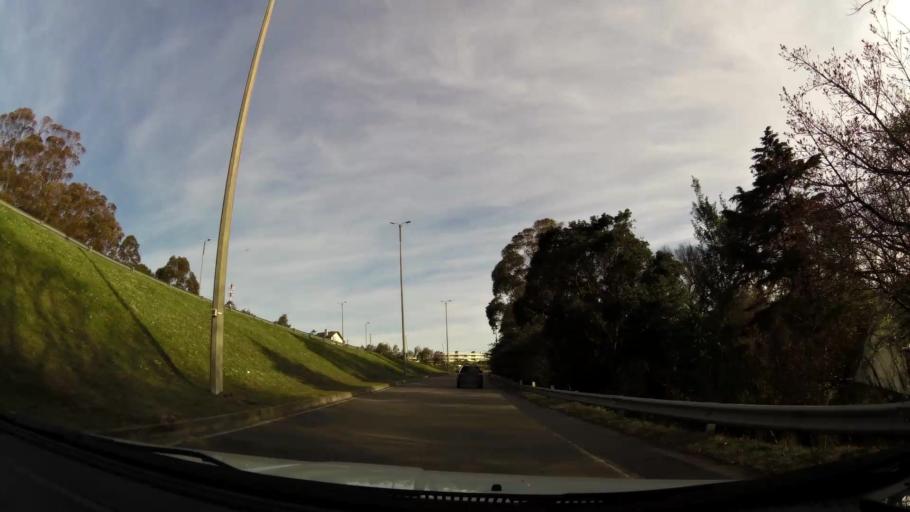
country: UY
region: Maldonado
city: Maldonado
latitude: -34.8873
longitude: -55.0393
